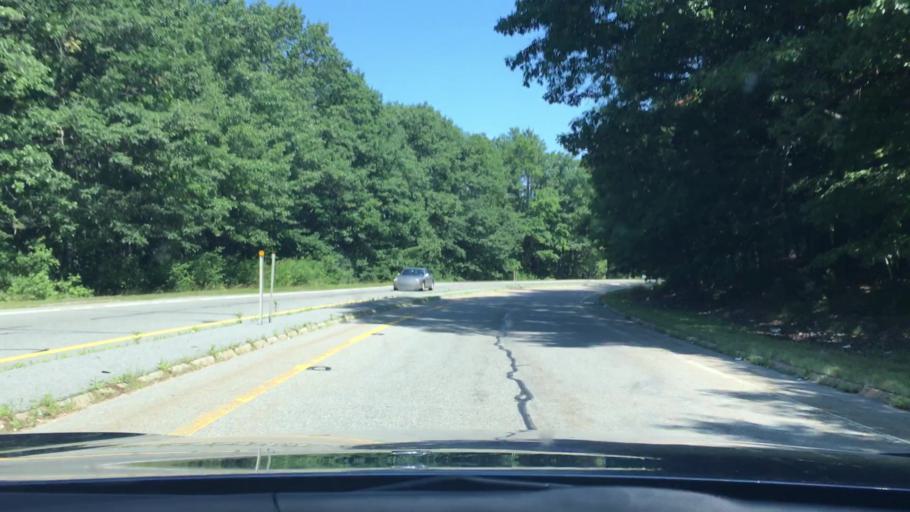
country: US
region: Massachusetts
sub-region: Middlesex County
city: Billerica
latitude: 42.5600
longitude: -71.2996
